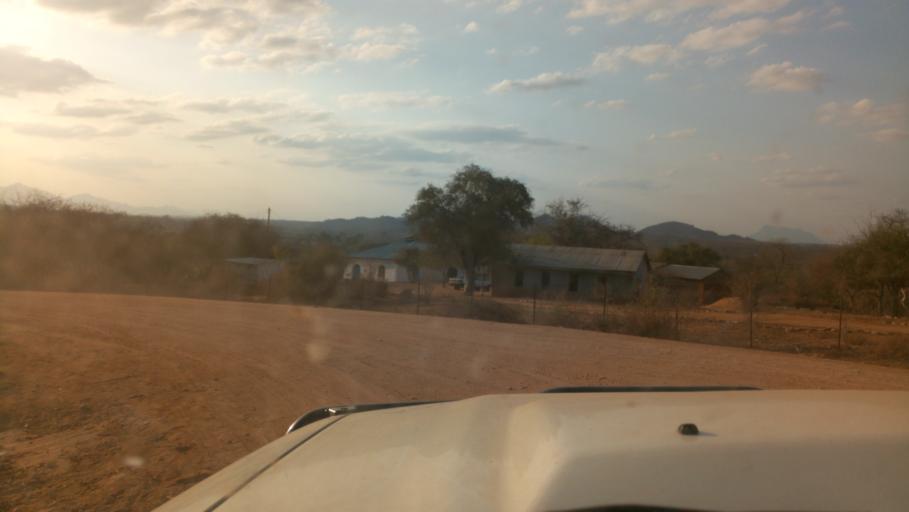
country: KE
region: Kitui
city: Kitui
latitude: -1.6670
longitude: 38.3241
